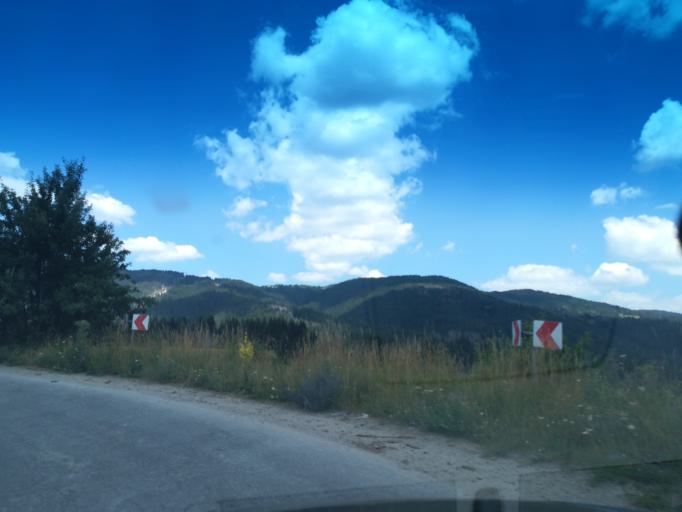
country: BG
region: Smolyan
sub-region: Obshtina Chepelare
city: Chepelare
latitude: 41.6731
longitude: 24.7818
